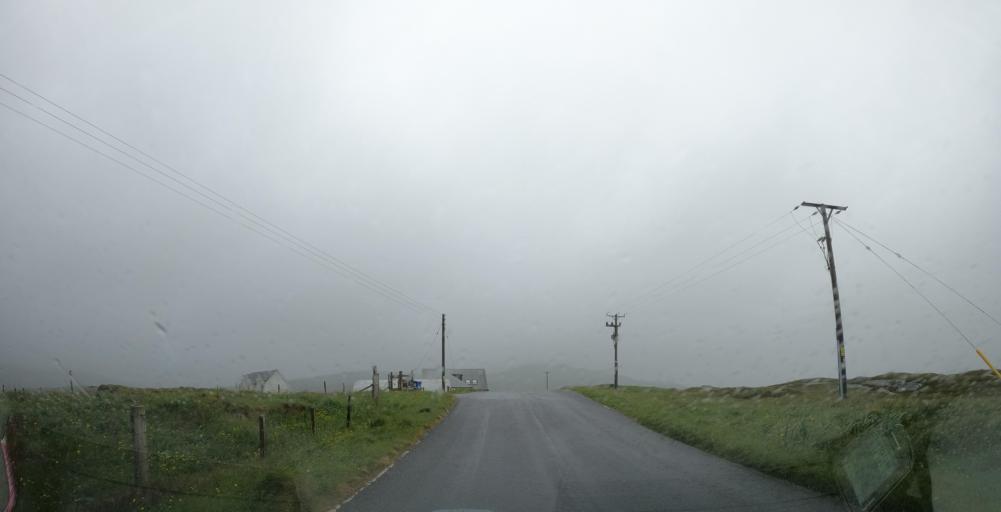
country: GB
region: Scotland
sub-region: Eilean Siar
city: Barra
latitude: 57.0090
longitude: -7.4190
